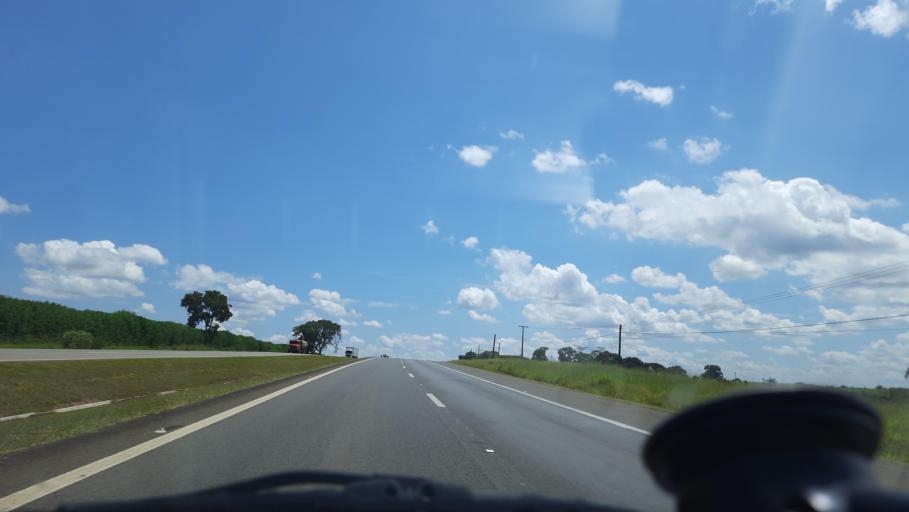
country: BR
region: Sao Paulo
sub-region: Moji-Guacu
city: Mogi-Gaucu
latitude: -22.2580
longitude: -46.9767
